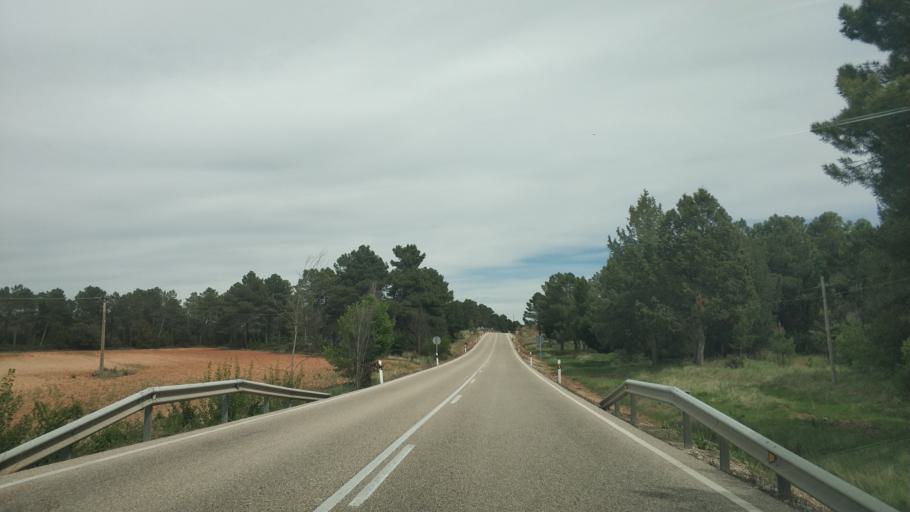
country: ES
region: Castille and Leon
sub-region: Provincia de Soria
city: Valdenebro
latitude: 41.5641
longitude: -2.9847
